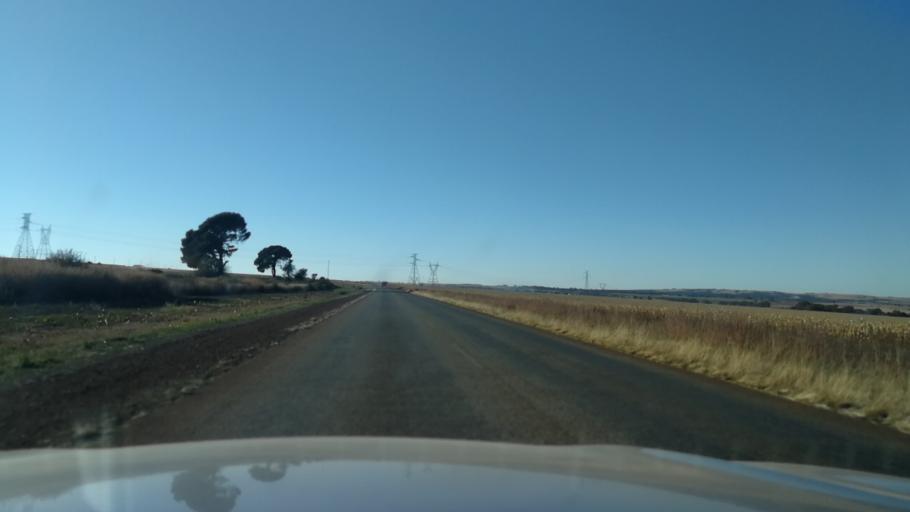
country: ZA
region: North-West
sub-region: Bojanala Platinum District Municipality
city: Rustenburg
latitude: -25.9948
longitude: 27.2946
